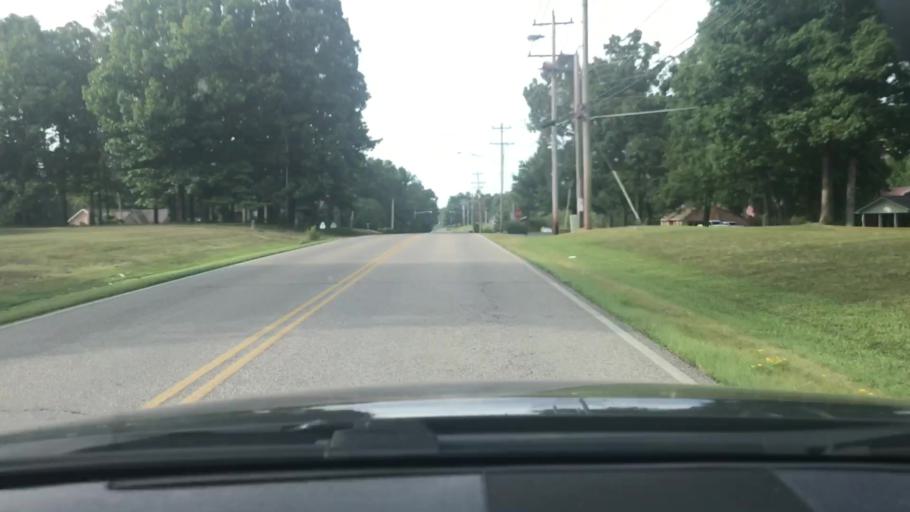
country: US
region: Tennessee
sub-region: Dickson County
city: White Bluff
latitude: 36.0909
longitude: -87.2137
